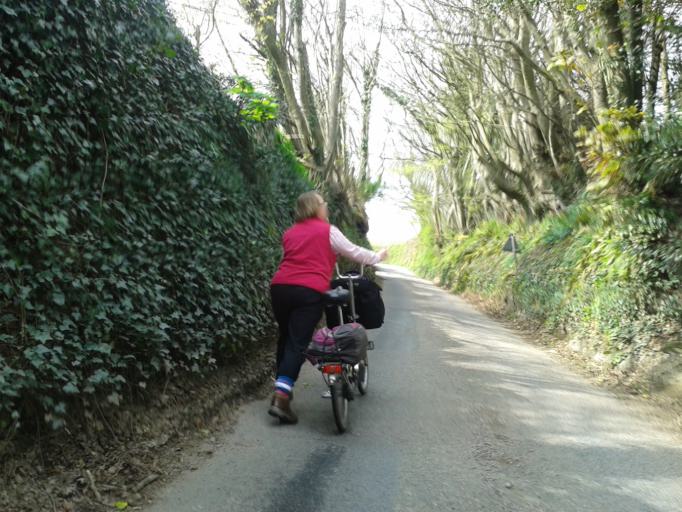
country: GB
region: England
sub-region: Devon
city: Braunton
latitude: 51.1152
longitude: -4.1644
